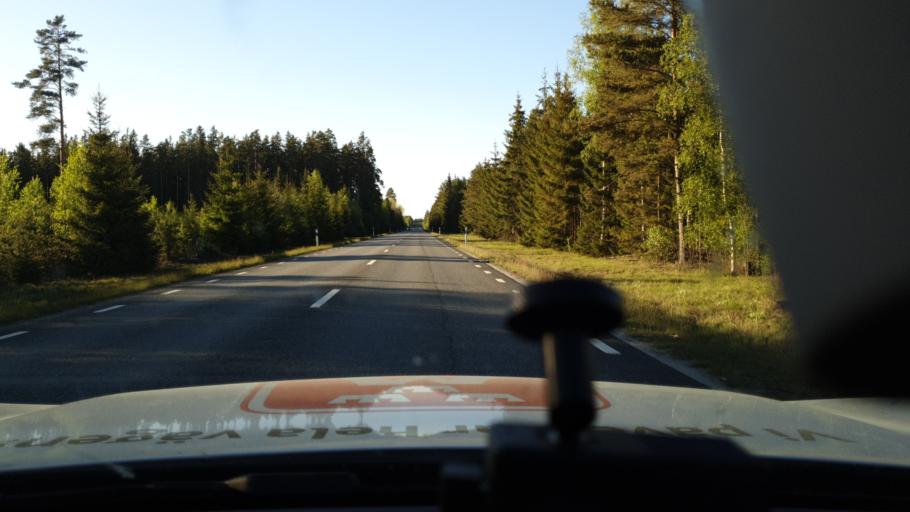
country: SE
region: Joenkoeping
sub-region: Eksjo Kommun
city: Eksjoe
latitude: 57.6194
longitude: 14.9703
